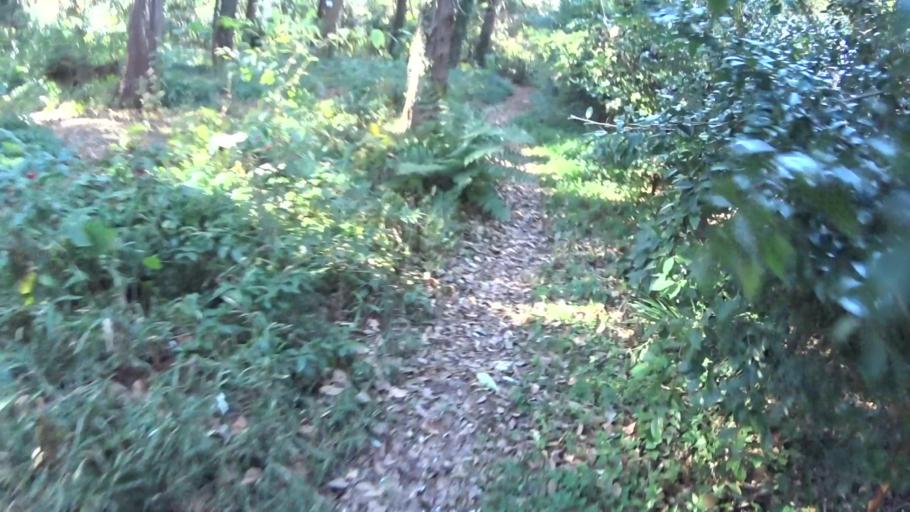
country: JP
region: Tokyo
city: Tokyo
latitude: 35.7223
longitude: 139.7423
